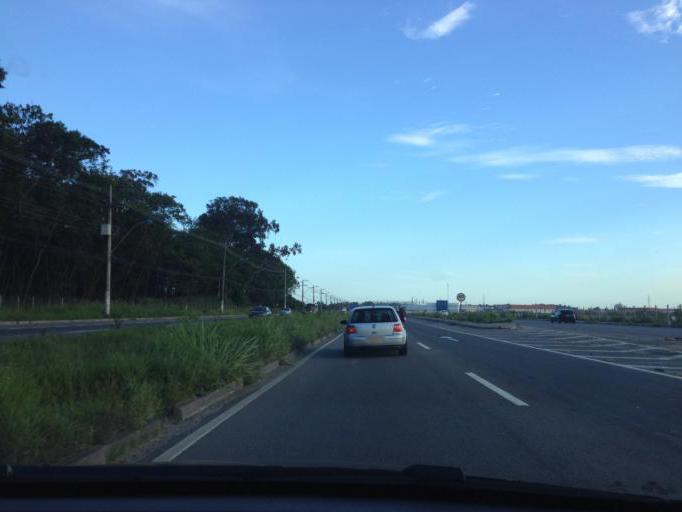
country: BR
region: Espirito Santo
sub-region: Vitoria
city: Vitoria
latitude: -20.3612
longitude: -40.3309
